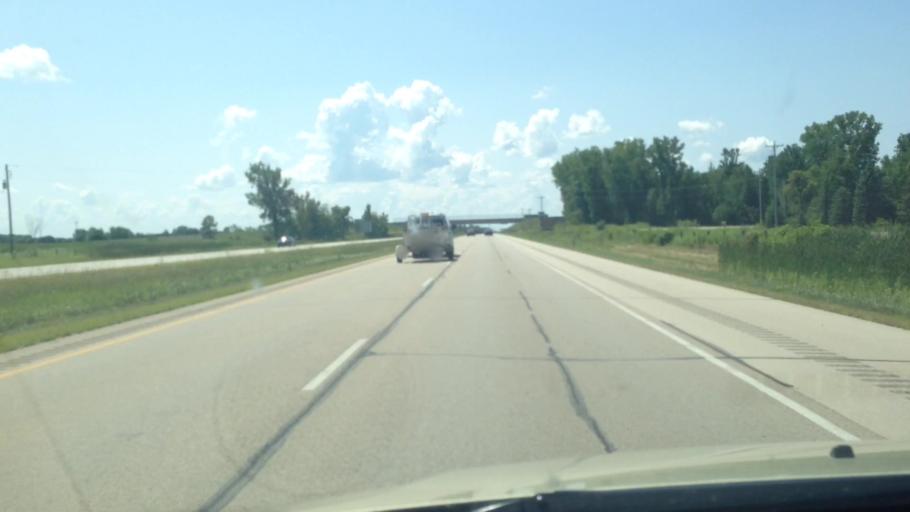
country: US
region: Wisconsin
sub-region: Brown County
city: Suamico
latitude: 44.7552
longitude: -88.0512
